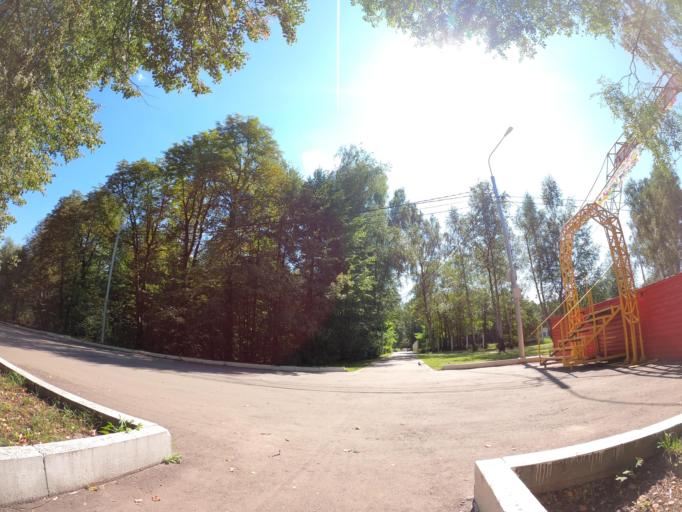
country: RU
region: Moskovskaya
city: Stupino
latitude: 54.8829
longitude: 38.0896
